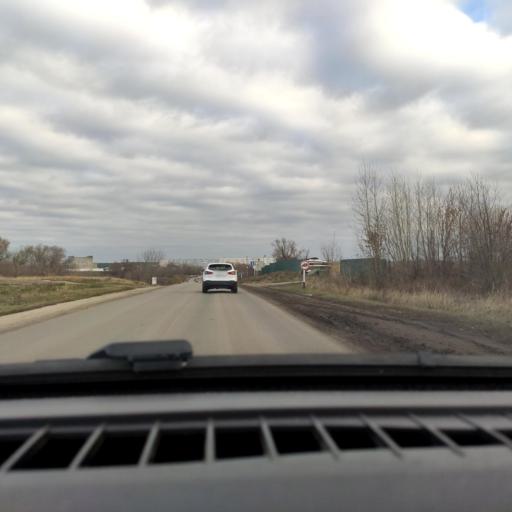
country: RU
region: Voronezj
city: Shilovo
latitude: 51.5393
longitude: 39.0767
